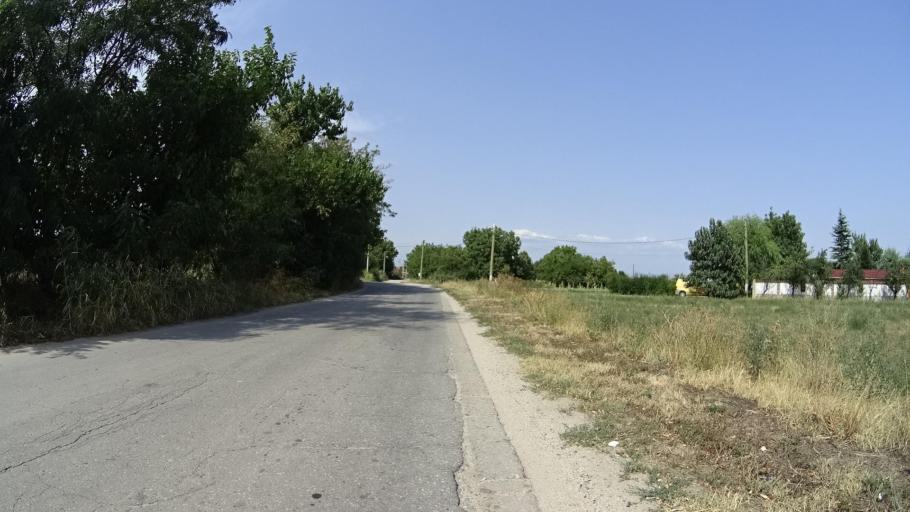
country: BG
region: Plovdiv
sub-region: Obshtina Kaloyanovo
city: Kaloyanovo
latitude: 42.2632
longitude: 24.8011
